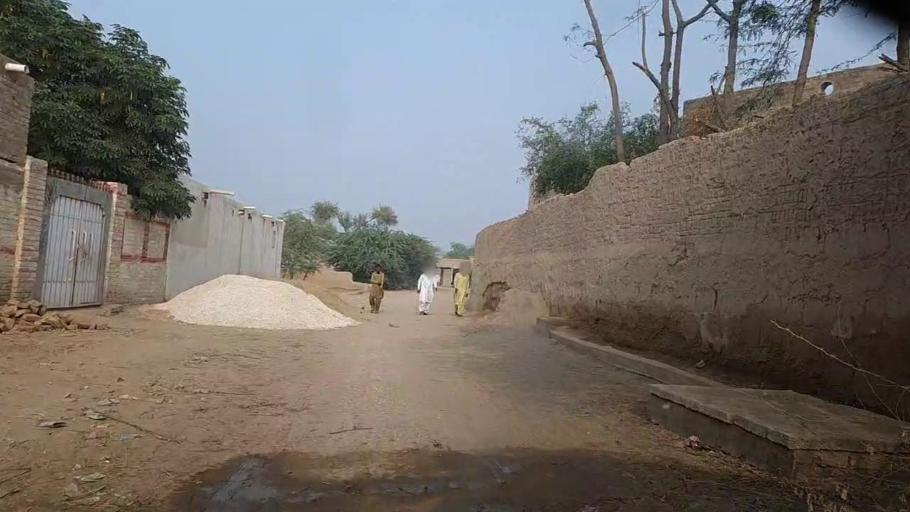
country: PK
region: Sindh
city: Bozdar
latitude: 27.1501
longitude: 68.6722
